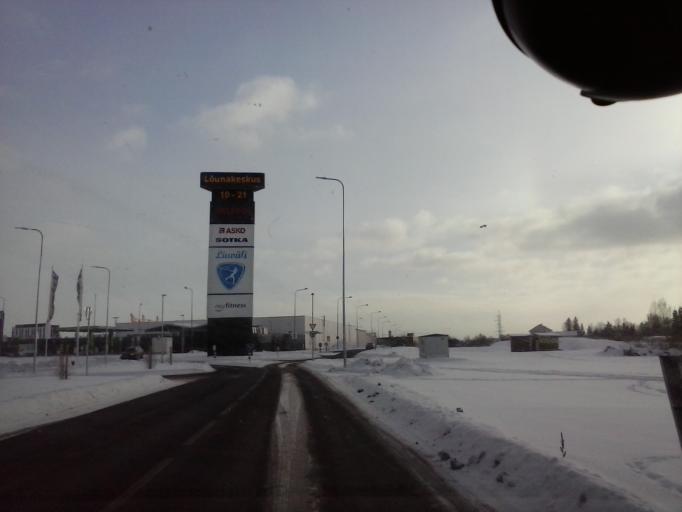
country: EE
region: Tartu
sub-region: Tartu linn
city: Tartu
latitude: 58.3631
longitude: 26.6749
